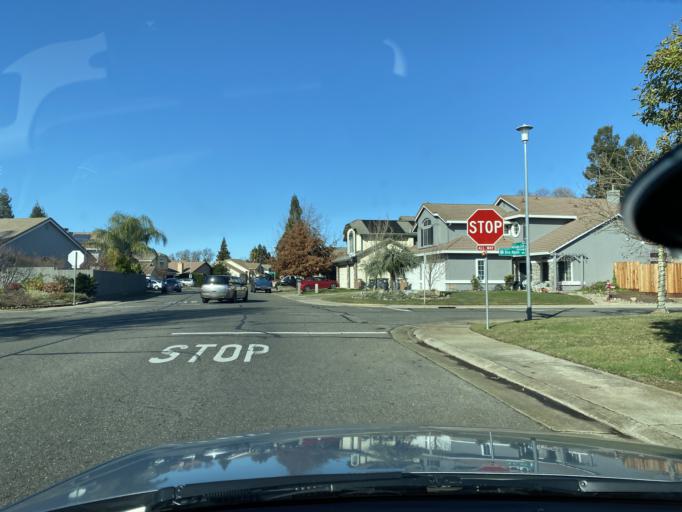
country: US
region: California
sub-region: Sacramento County
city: Elk Grove
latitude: 38.4355
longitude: -121.3830
